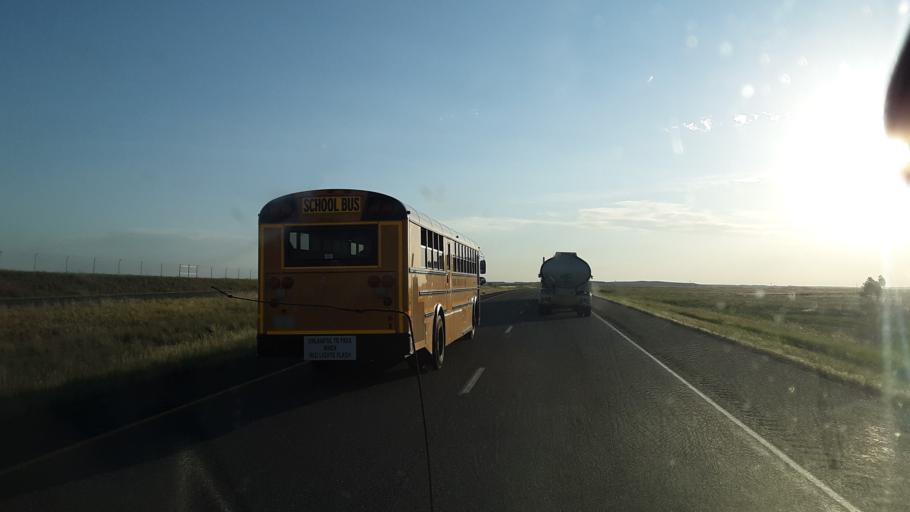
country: US
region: Montana
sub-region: Big Horn County
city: Hardin
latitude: 45.7464
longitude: -107.6443
